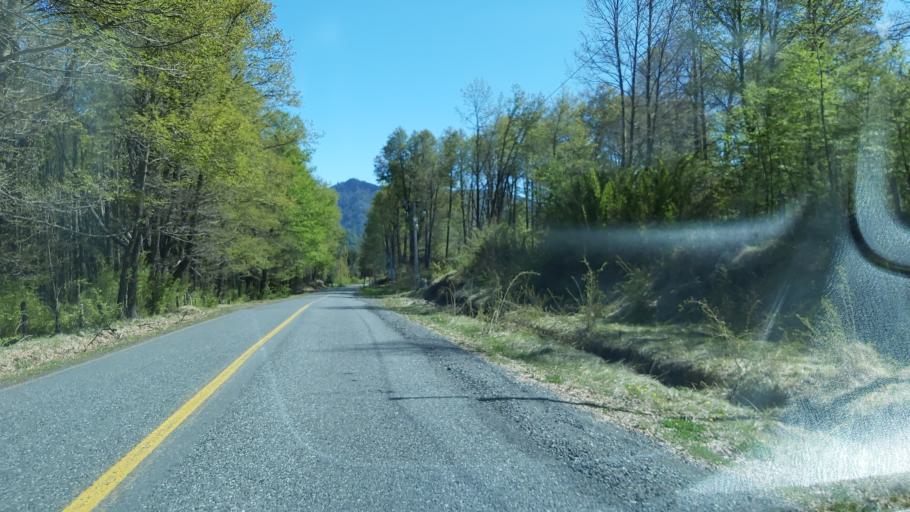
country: CL
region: Araucania
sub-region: Provincia de Cautin
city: Vilcun
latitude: -38.4662
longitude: -71.5197
